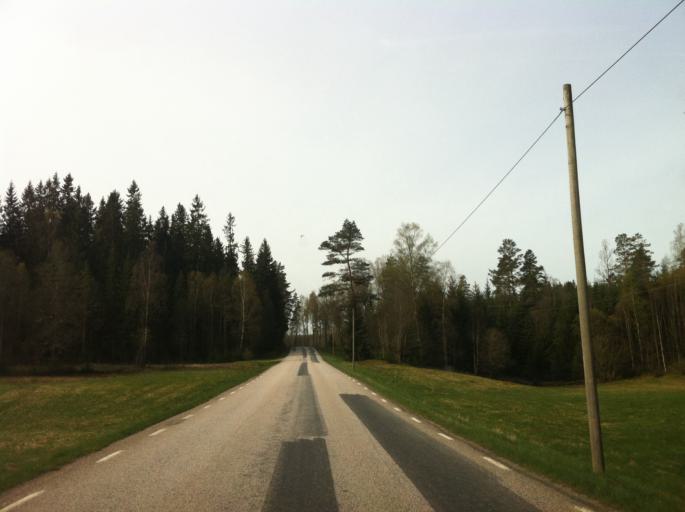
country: SE
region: Vaestra Goetaland
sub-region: Bollebygds Kommun
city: Bollebygd
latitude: 57.7485
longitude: 12.6102
